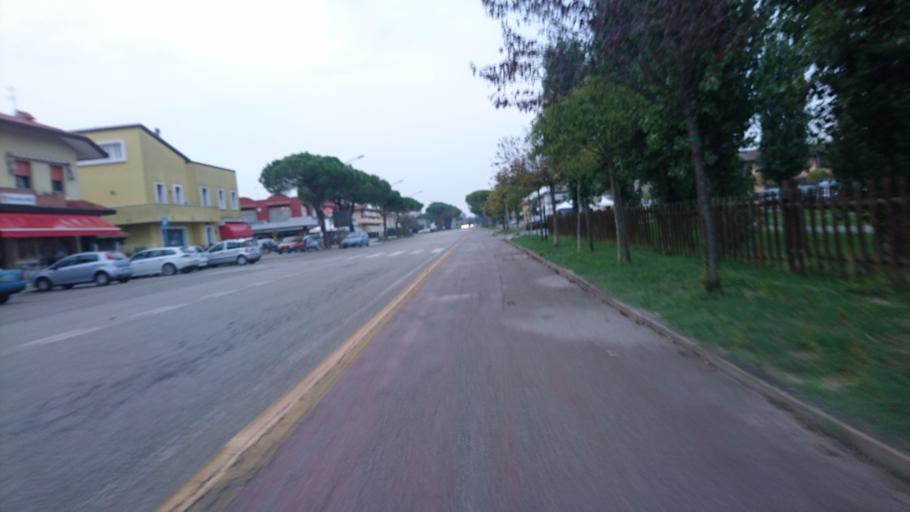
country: IT
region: Veneto
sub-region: Provincia di Rovigo
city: Ca' Tiepolo
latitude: 44.9448
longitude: 12.3332
